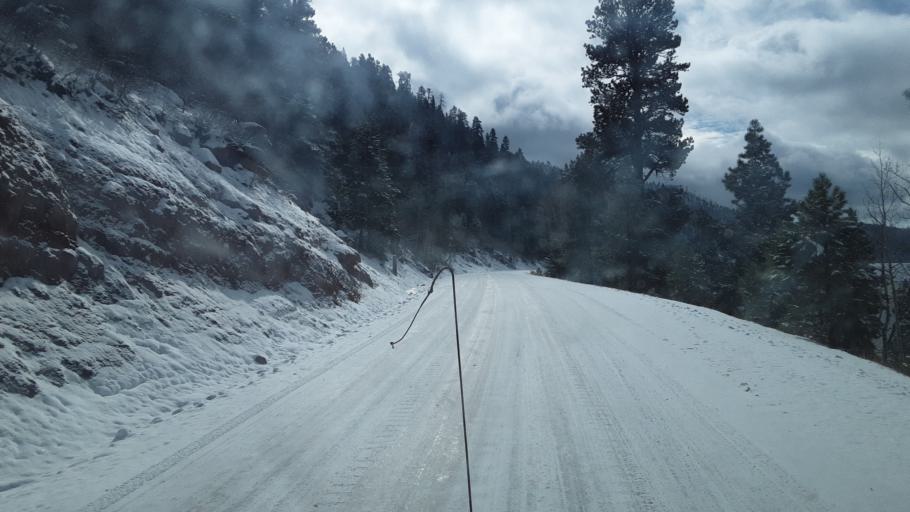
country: US
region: Colorado
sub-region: La Plata County
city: Bayfield
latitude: 37.3934
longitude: -107.6572
